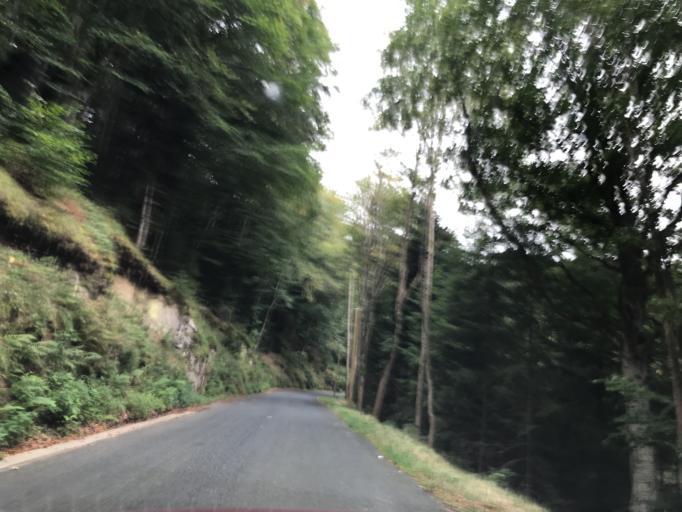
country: FR
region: Rhone-Alpes
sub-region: Departement de la Loire
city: Sail-sous-Couzan
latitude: 45.6851
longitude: 3.9058
